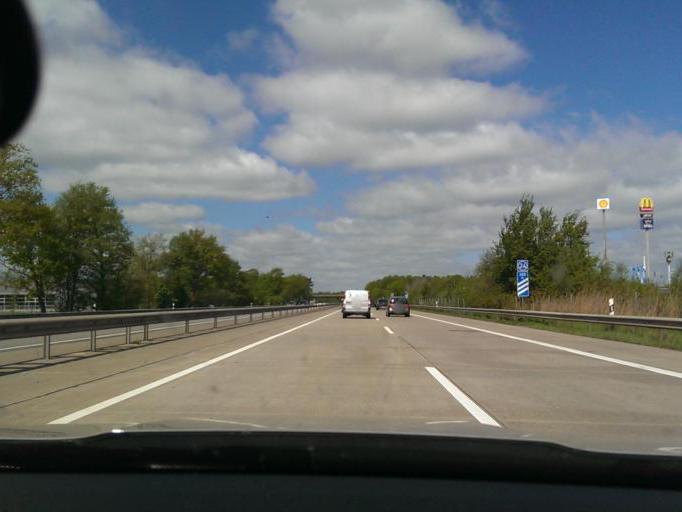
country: DE
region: Lower Saxony
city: Achim
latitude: 53.0173
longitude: 9.0722
